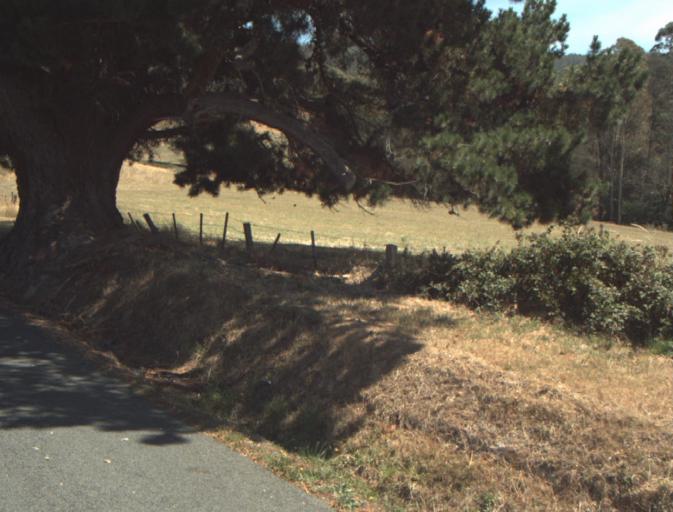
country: AU
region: Tasmania
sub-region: Launceston
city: Mayfield
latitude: -41.2661
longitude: 147.1328
